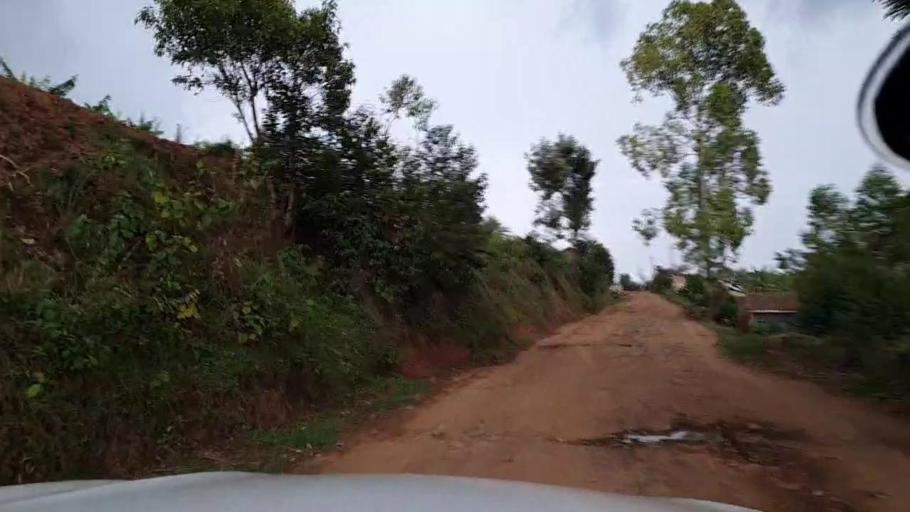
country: BI
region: Kayanza
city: Kayanza
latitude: -2.7887
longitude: 29.5282
